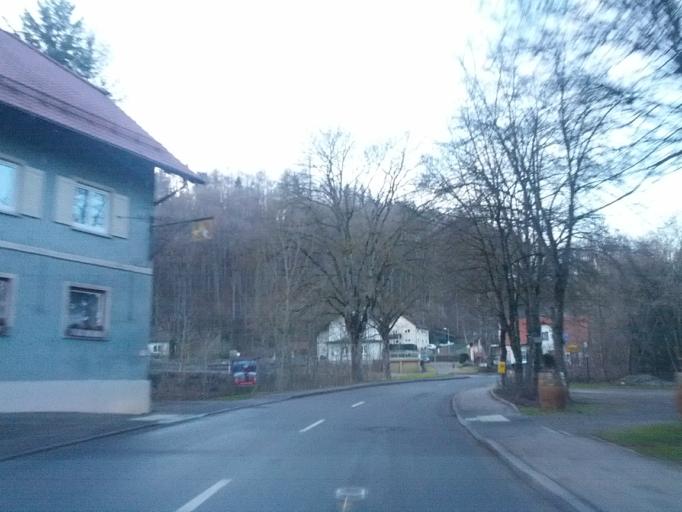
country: DE
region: Baden-Wuerttemberg
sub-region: Tuebingen Region
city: Aitrach
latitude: 47.9415
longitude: 10.0816
